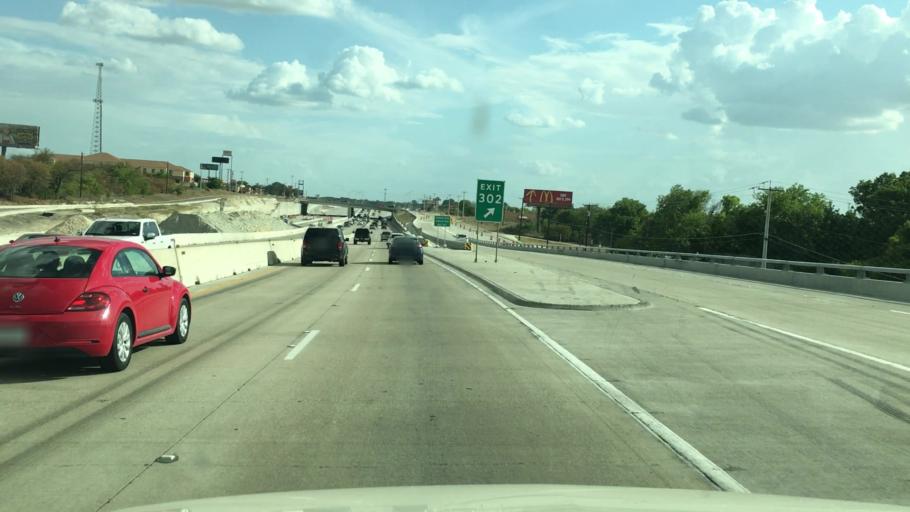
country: US
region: Texas
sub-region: Bell County
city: Temple
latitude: 31.1193
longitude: -97.3535
